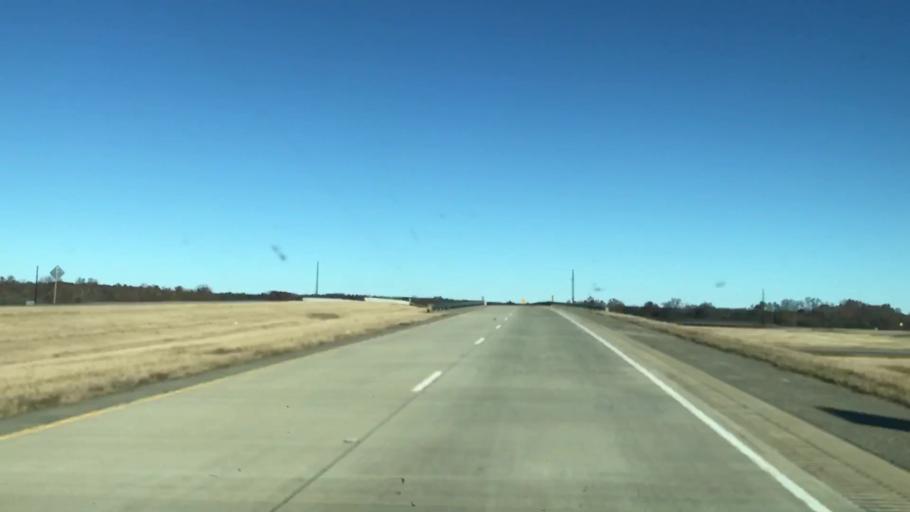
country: US
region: Louisiana
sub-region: Caddo Parish
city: Vivian
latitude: 32.8954
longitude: -93.8606
